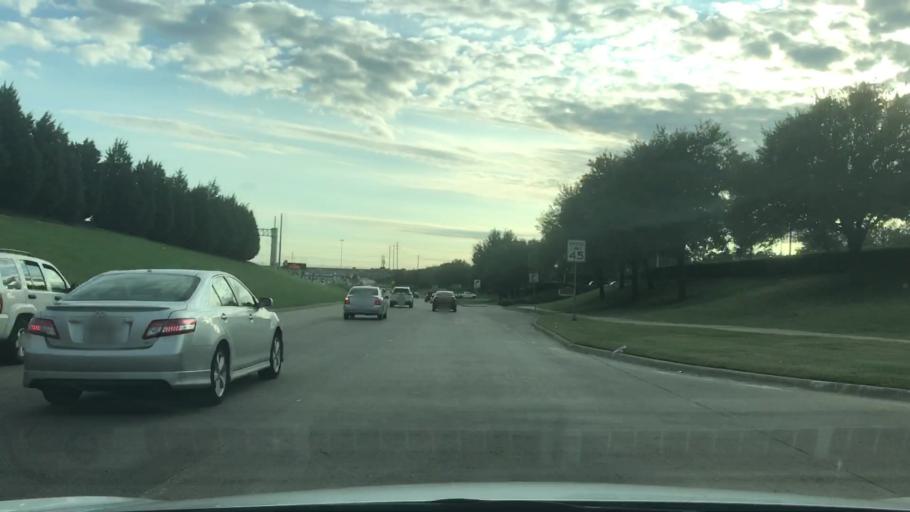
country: US
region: Texas
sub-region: Dallas County
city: Coppell
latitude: 32.8899
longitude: -96.9818
